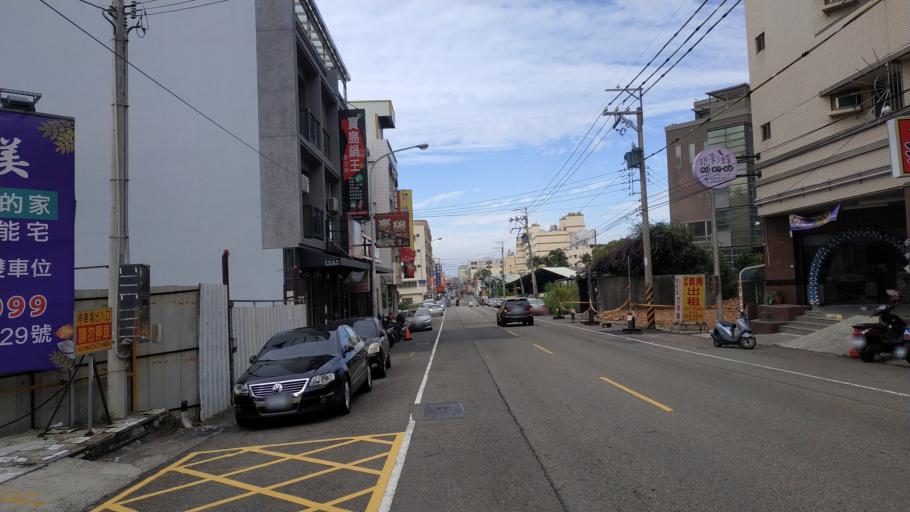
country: TW
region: Taiwan
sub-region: Taichung City
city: Taichung
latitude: 24.2233
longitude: 120.5774
